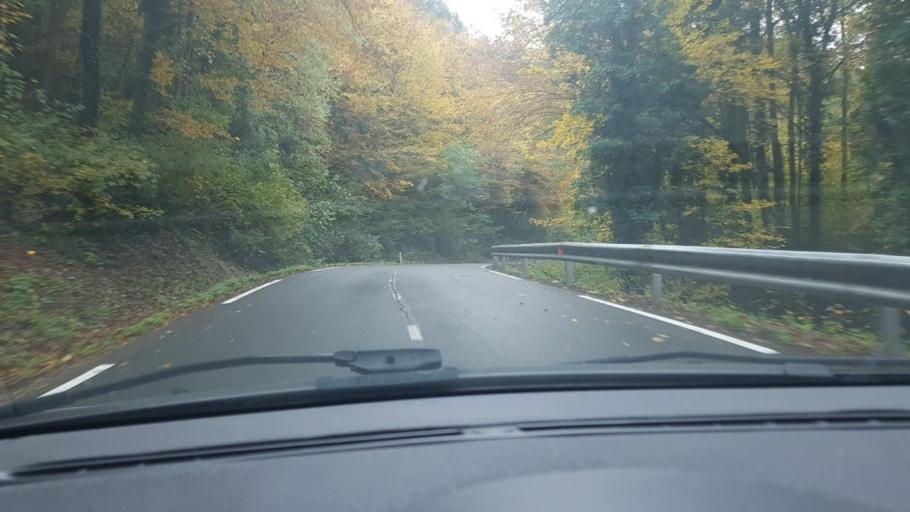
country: SI
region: Rogatec
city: Rogatec
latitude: 46.2764
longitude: 15.7104
